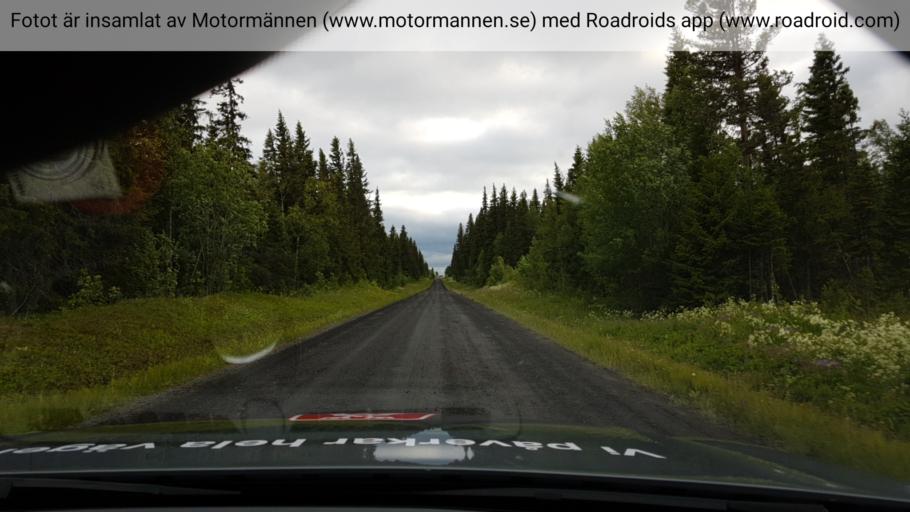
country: SE
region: Jaemtland
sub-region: OEstersunds Kommun
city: Lit
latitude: 63.6222
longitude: 15.0181
